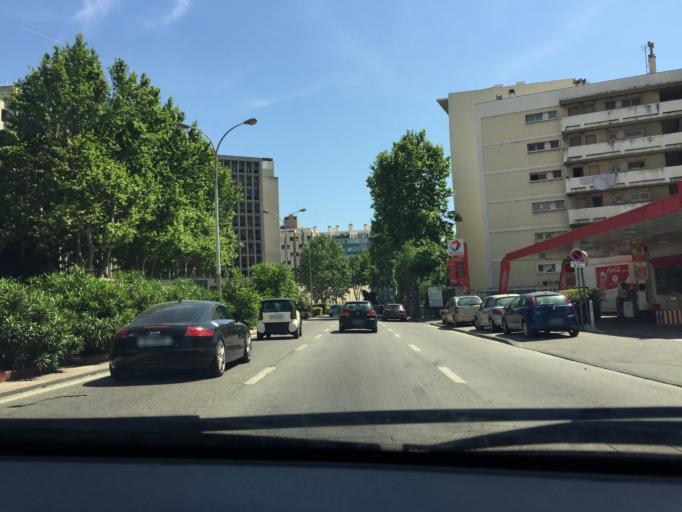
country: FR
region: Provence-Alpes-Cote d'Azur
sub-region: Departement des Bouches-du-Rhone
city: Marseille 05
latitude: 43.2885
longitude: 5.4002
